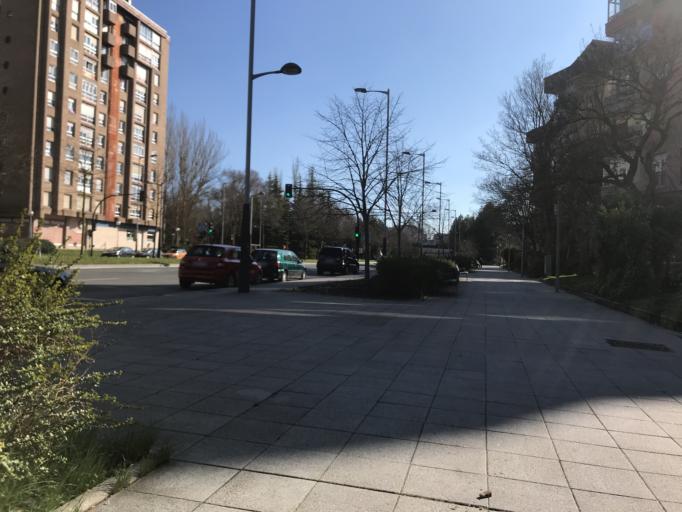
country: ES
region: Basque Country
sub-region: Provincia de Alava
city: Gasteiz / Vitoria
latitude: 42.8536
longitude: -2.6578
